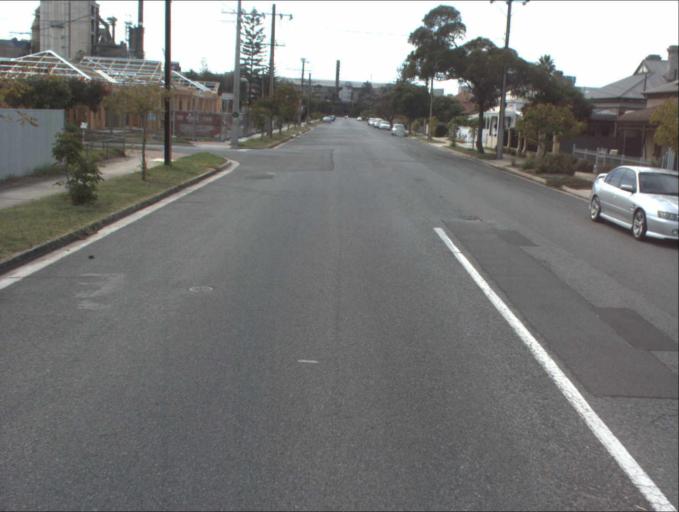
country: AU
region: South Australia
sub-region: Port Adelaide Enfield
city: Birkenhead
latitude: -34.8334
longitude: 138.4973
